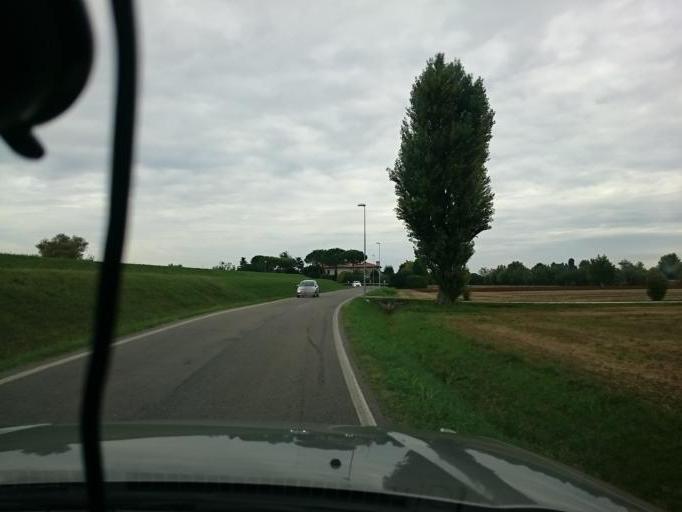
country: IT
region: Veneto
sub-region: Provincia di Padova
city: Saccolongo
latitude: 45.4179
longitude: 11.7487
